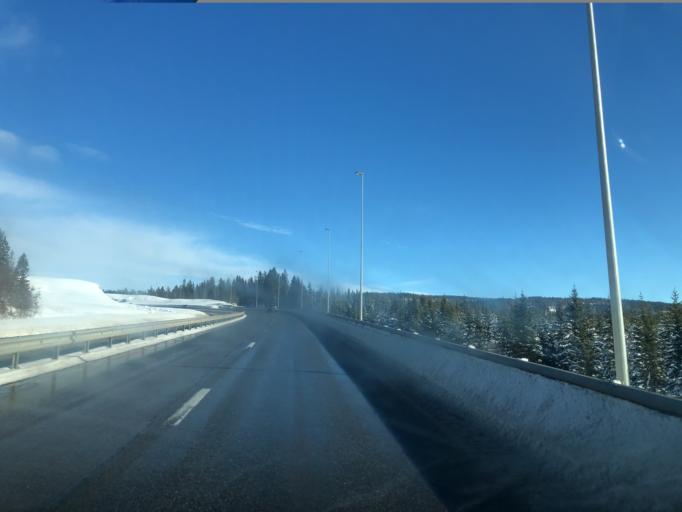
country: NO
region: Oppland
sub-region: Gran
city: Jaren
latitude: 60.4389
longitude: 10.6043
